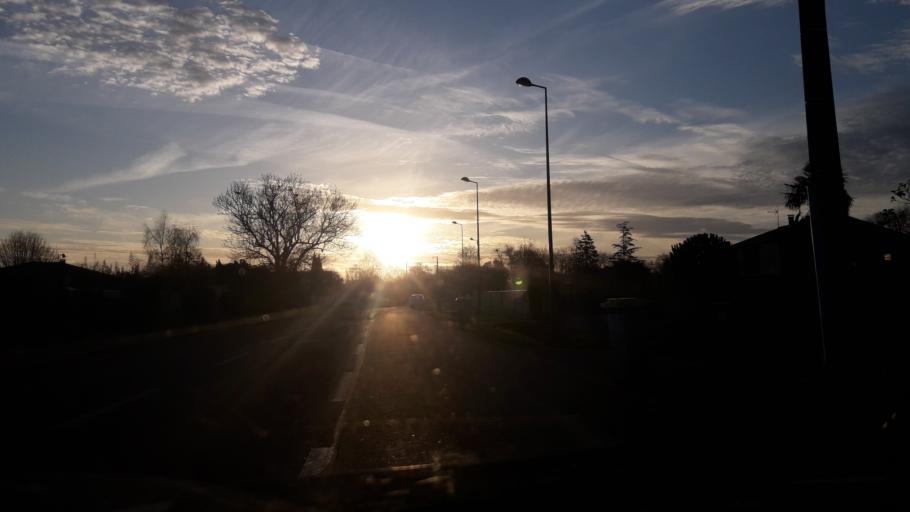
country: FR
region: Midi-Pyrenees
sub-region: Departement de la Haute-Garonne
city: Labastidette
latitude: 43.4858
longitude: 1.2394
